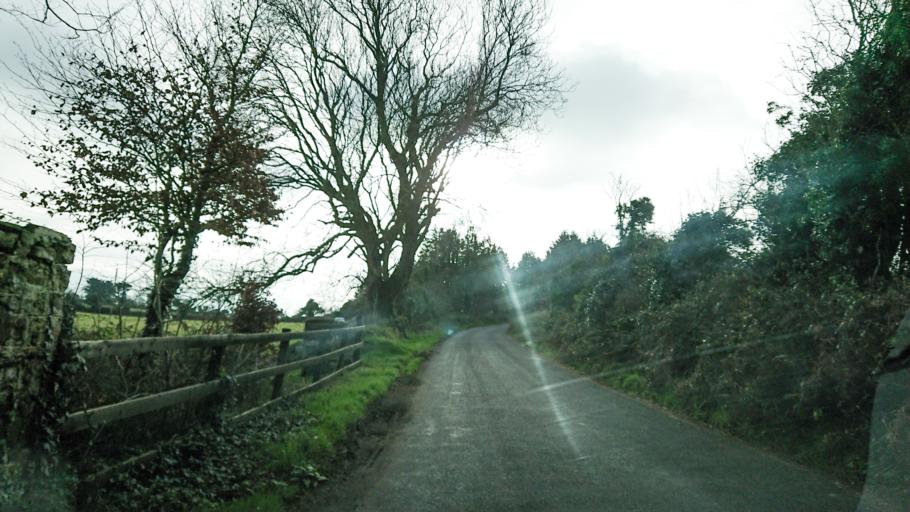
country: IE
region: Munster
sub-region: Waterford
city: Tra Mhor
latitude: 52.1768
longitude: -7.1748
